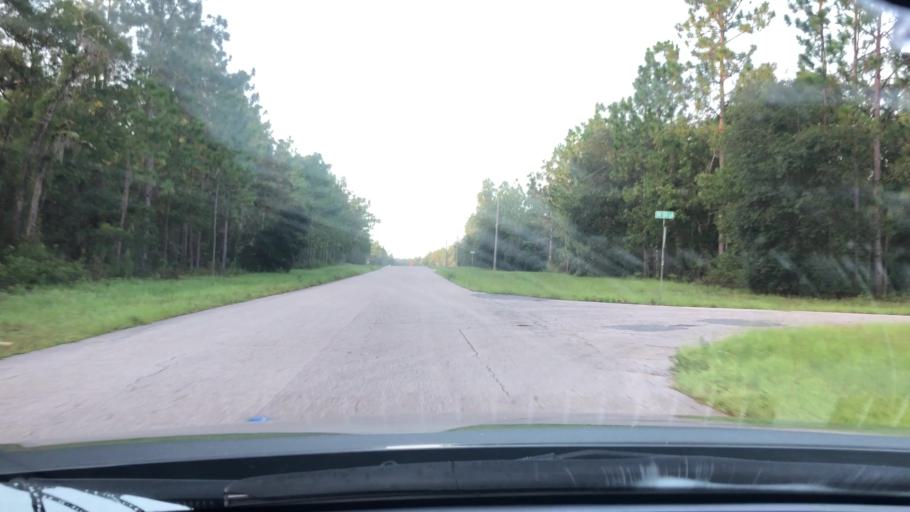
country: US
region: Florida
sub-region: Marion County
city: Belleview
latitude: 29.0288
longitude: -82.2403
